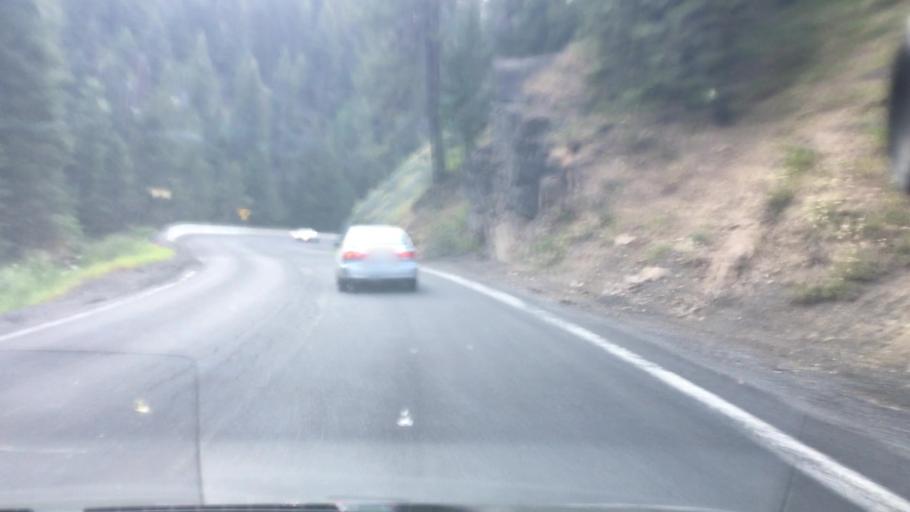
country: US
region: Idaho
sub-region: Valley County
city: McCall
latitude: 44.9606
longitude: -116.1725
